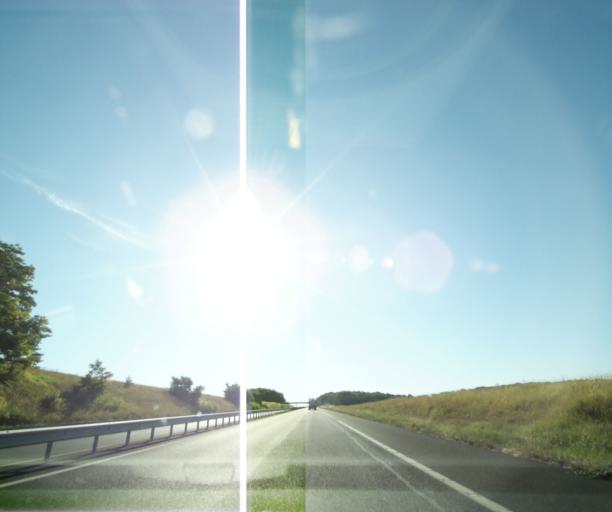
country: FR
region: Bourgogne
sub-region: Departement de l'Yonne
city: Thorigny-sur-Oreuse
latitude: 48.2357
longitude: 3.4135
